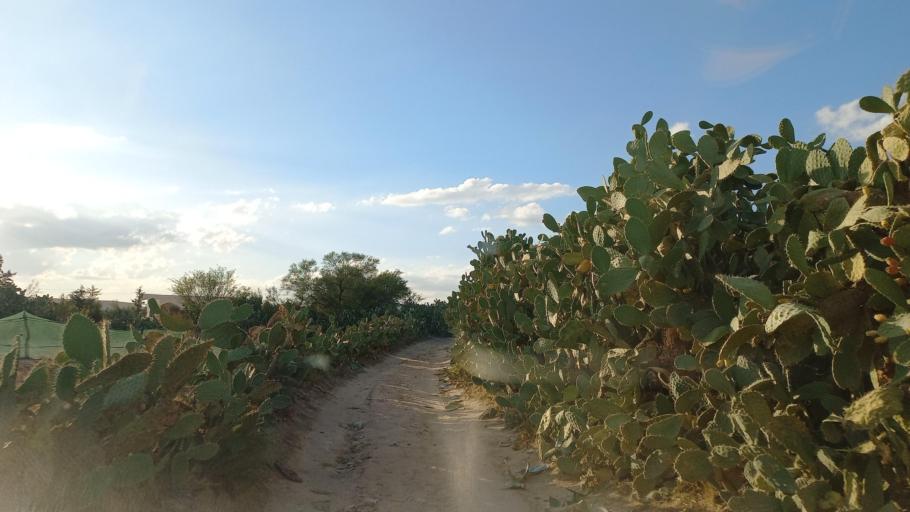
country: TN
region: Al Qasrayn
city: Sbiba
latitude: 35.3877
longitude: 9.0436
